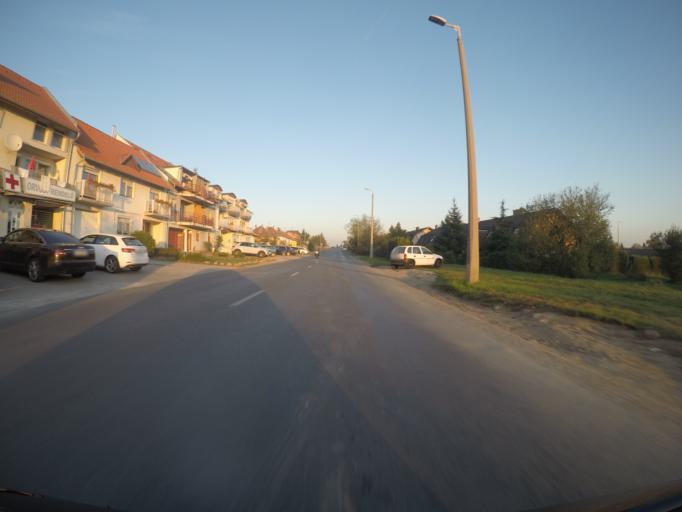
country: HU
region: Baranya
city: Pellerd
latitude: 46.0657
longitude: 18.1688
